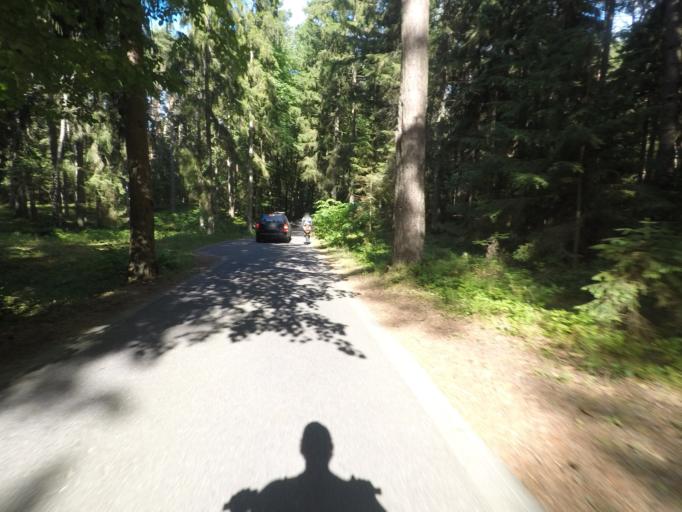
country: LT
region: Klaipedos apskritis
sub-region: Klaipeda
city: Klaipeda
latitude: 55.5422
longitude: 21.1131
